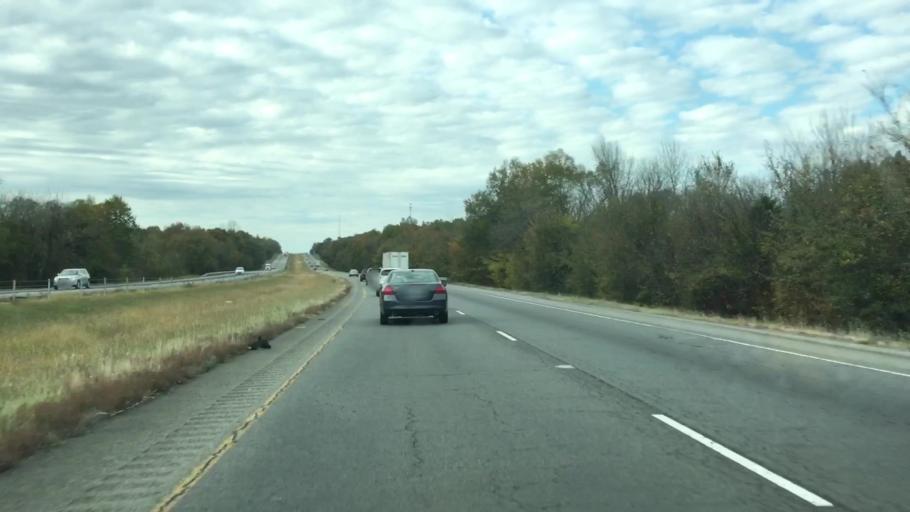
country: US
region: Arkansas
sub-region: Faulkner County
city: Conway
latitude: 35.1385
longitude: -92.5229
